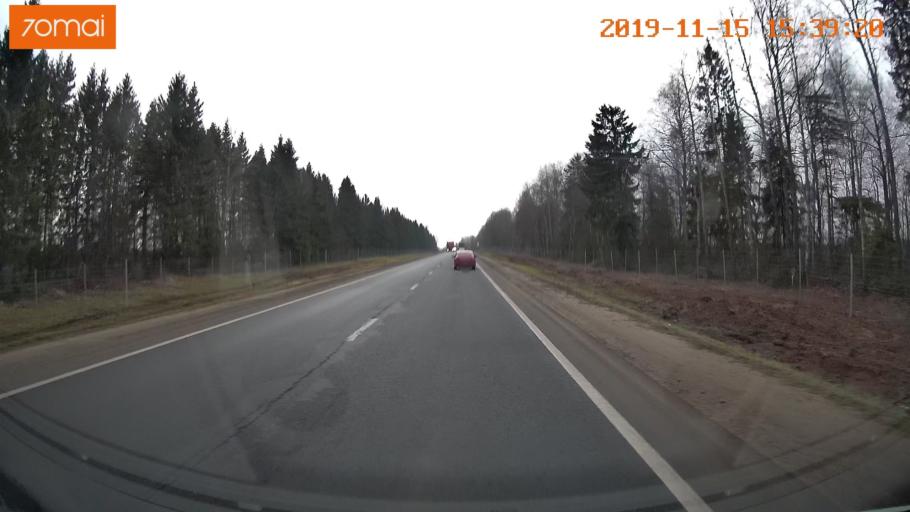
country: RU
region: Jaroslavl
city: Danilov
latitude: 58.0218
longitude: 40.0695
